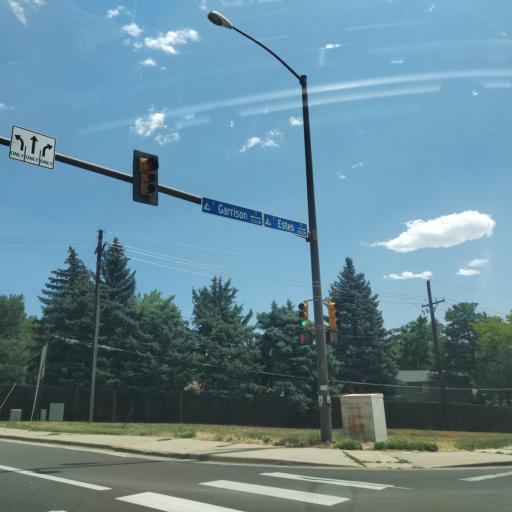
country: US
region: Colorado
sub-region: Jefferson County
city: Lakewood
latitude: 39.6728
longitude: -105.0953
